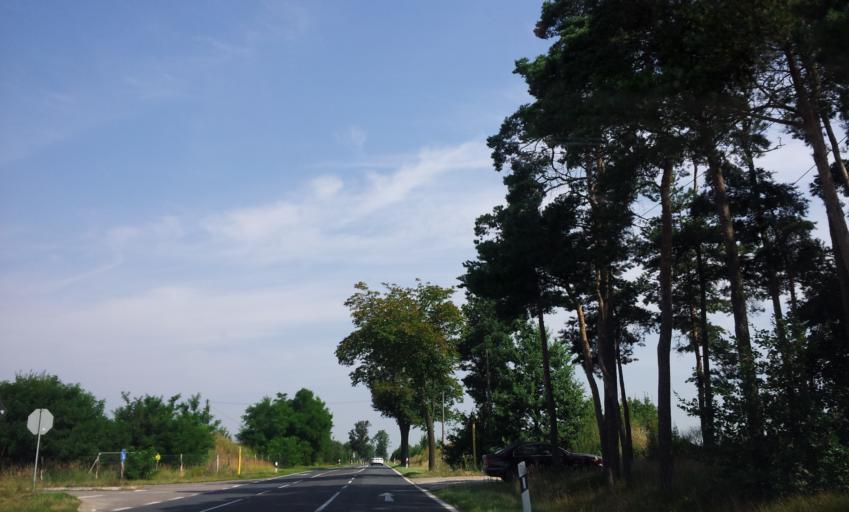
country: DE
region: Brandenburg
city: Linthe
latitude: 52.1433
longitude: 12.7893
